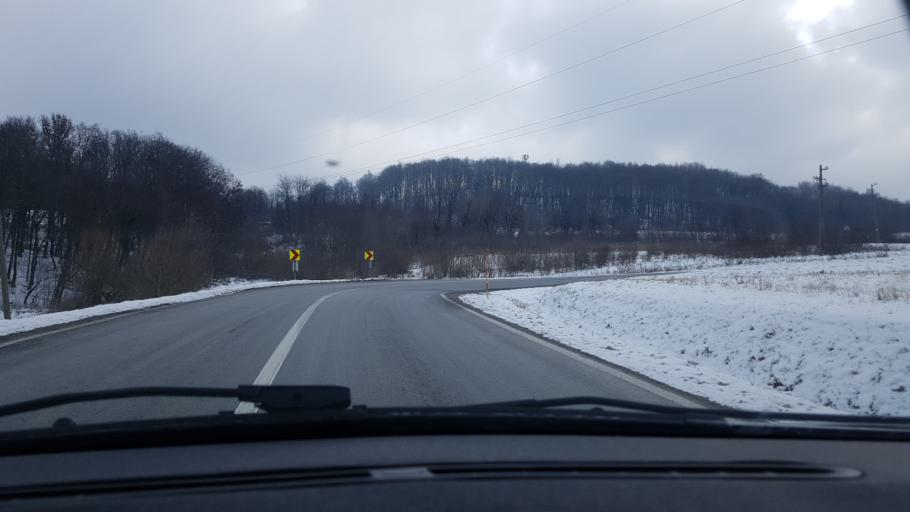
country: HR
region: Krapinsko-Zagorska
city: Mihovljan
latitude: 46.1683
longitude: 15.9771
